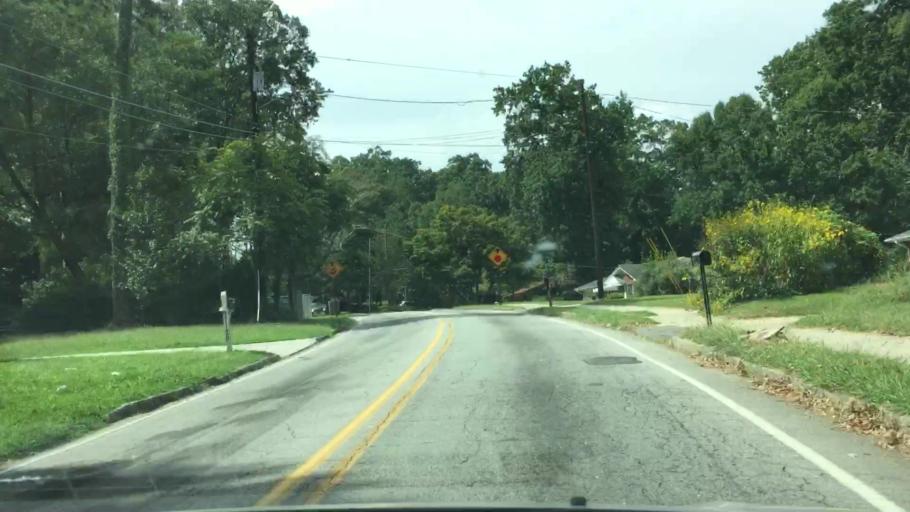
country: US
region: Georgia
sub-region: DeKalb County
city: Gresham Park
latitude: 33.7237
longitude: -84.3272
